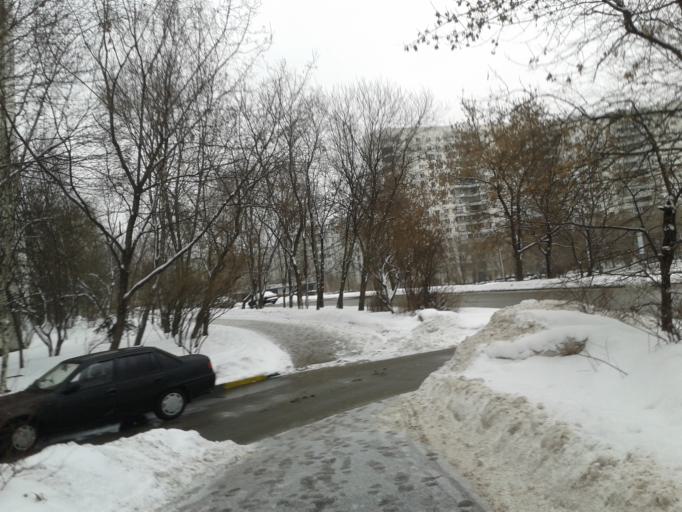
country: RU
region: Moscow
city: Strogino
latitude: 55.8051
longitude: 37.4091
